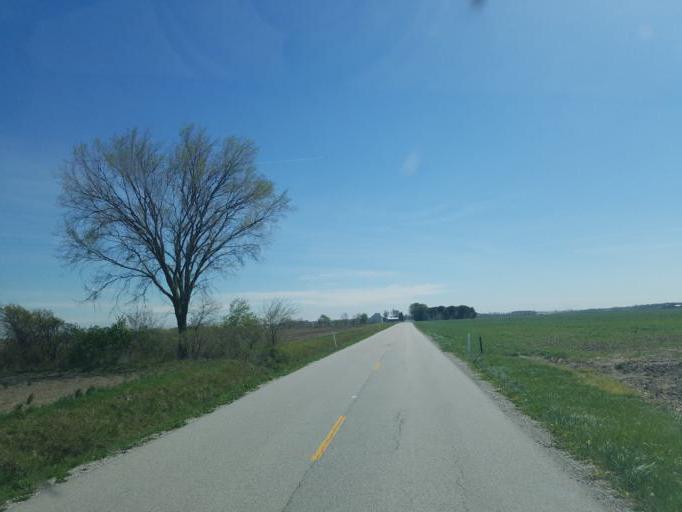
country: US
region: Ohio
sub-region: Huron County
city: Bellevue
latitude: 41.3196
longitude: -82.7930
